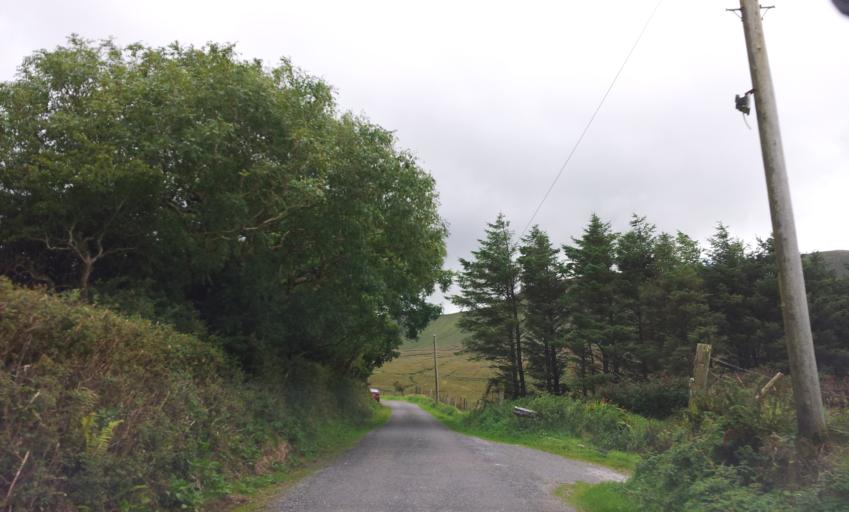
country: IE
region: Munster
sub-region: Ciarrai
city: Killorglin
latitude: 52.1958
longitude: -9.9302
